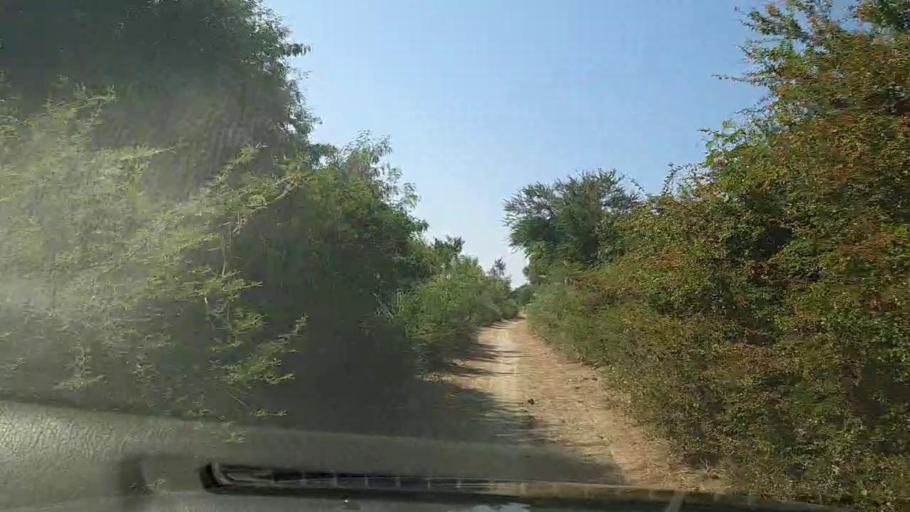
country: PK
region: Sindh
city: Mirpur Sakro
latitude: 24.5849
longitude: 67.8113
